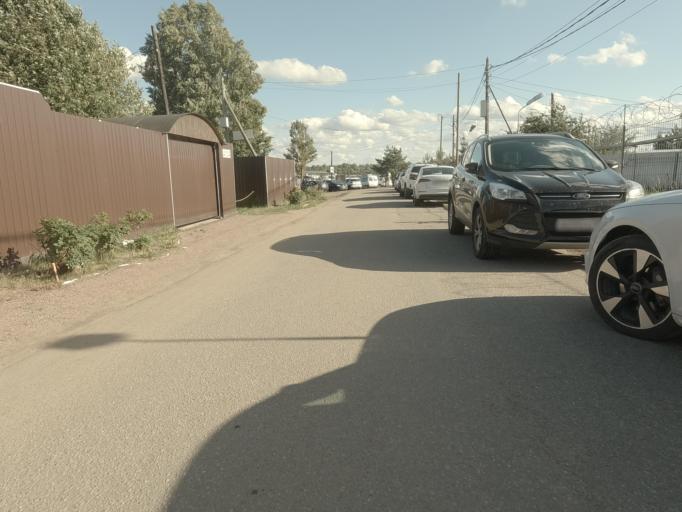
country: RU
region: Leningrad
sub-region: Volosovskiy Rayon
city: Shlissel'burg
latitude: 59.9585
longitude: 31.0315
